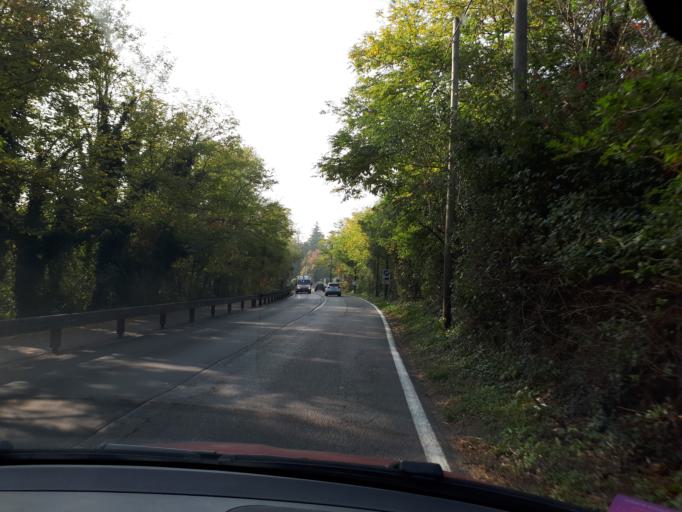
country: IT
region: Lombardy
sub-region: Provincia di Monza e Brianza
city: Lesmo
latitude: 45.6341
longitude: 9.2982
